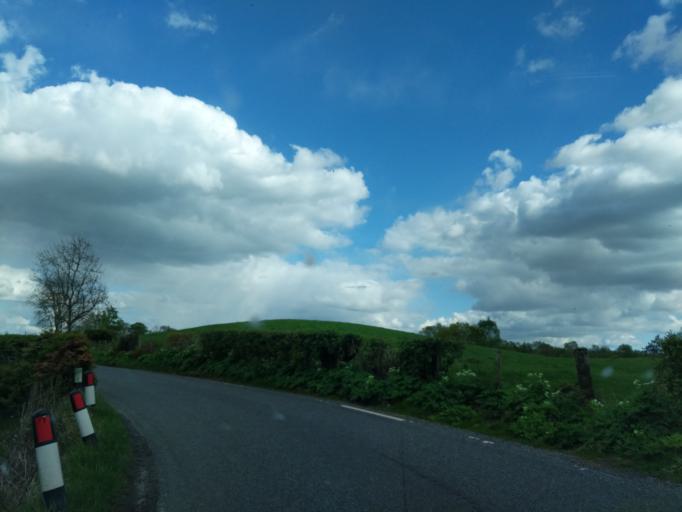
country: GB
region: Scotland
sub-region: Stirling
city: Callander
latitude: 56.1728
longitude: -4.2729
